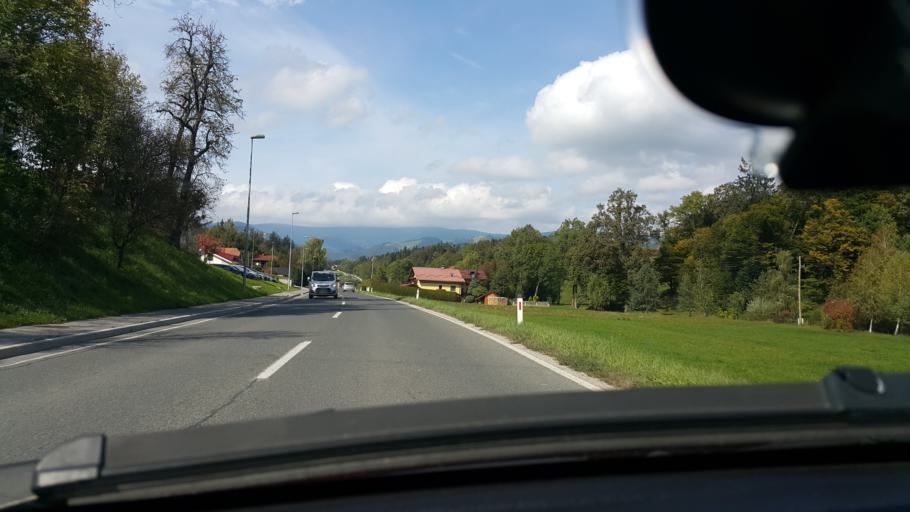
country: SI
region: Slovenska Konjice
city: Slovenske Konjice
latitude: 46.3537
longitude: 15.4001
